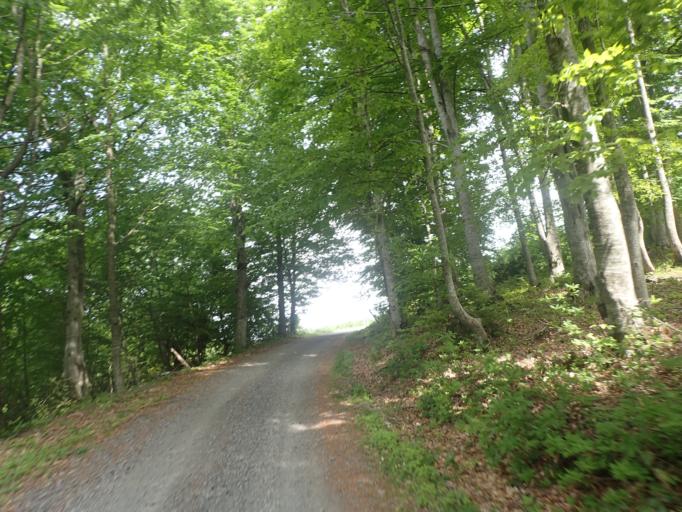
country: TR
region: Ordu
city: Tekkiraz
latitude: 40.9017
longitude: 37.0794
